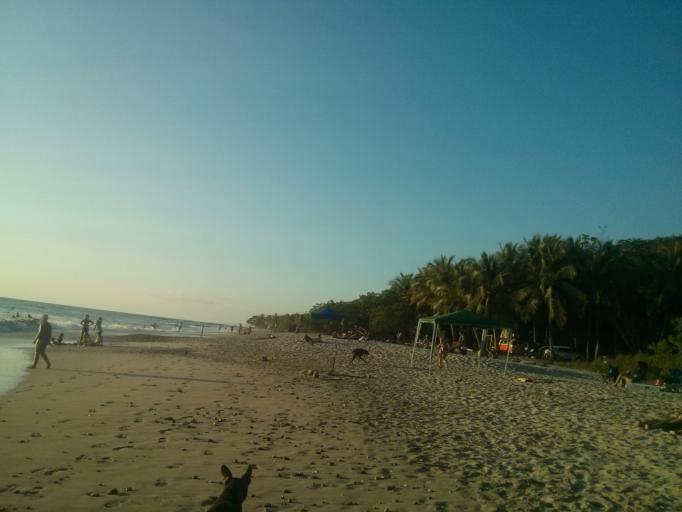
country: CR
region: Guanacaste
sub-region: Canton de Nandayure
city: Bejuco
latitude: 9.6312
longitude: -85.1575
